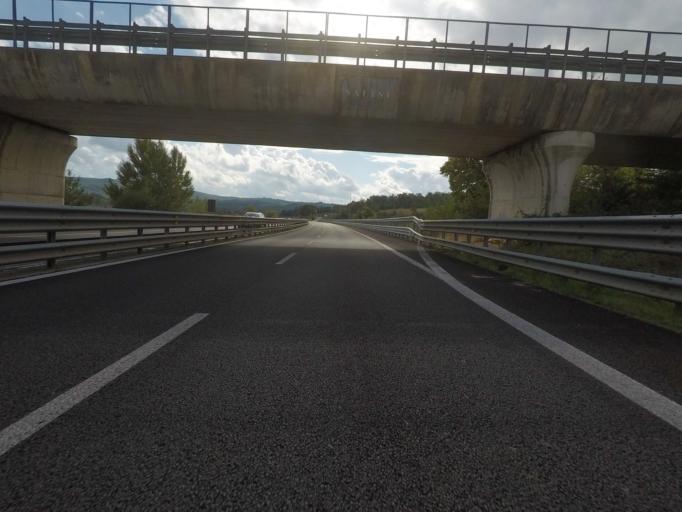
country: IT
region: Tuscany
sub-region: Provincia di Siena
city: Serre di Rapolano
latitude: 43.2577
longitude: 11.6326
